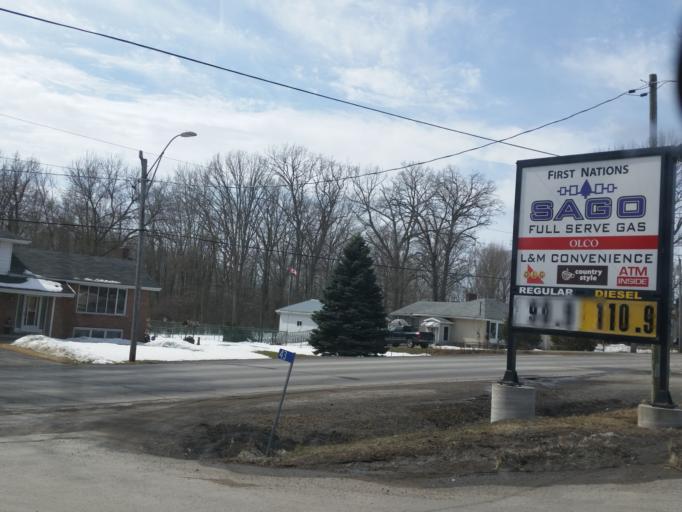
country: CA
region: Ontario
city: Deseronto
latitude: 44.1963
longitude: -77.0636
